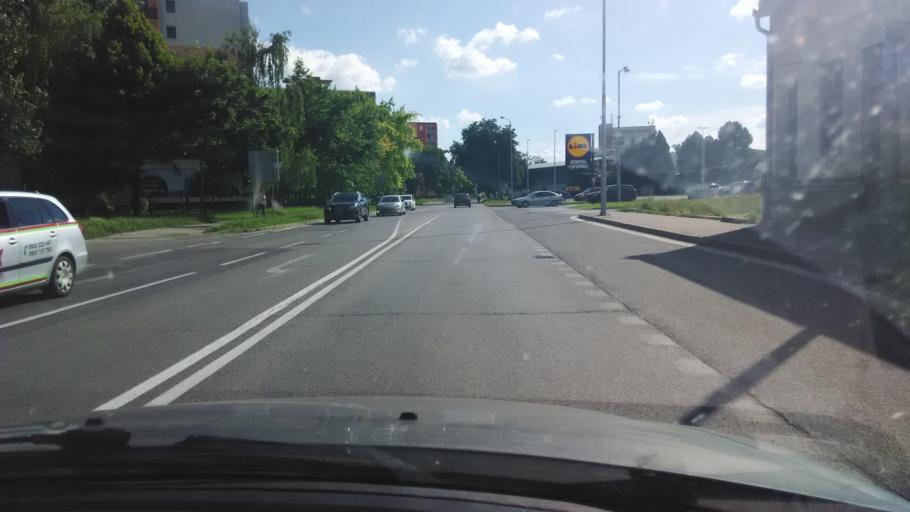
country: SK
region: Nitriansky
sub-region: Okres Nove Zamky
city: Nove Zamky
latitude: 47.9928
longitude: 18.1676
